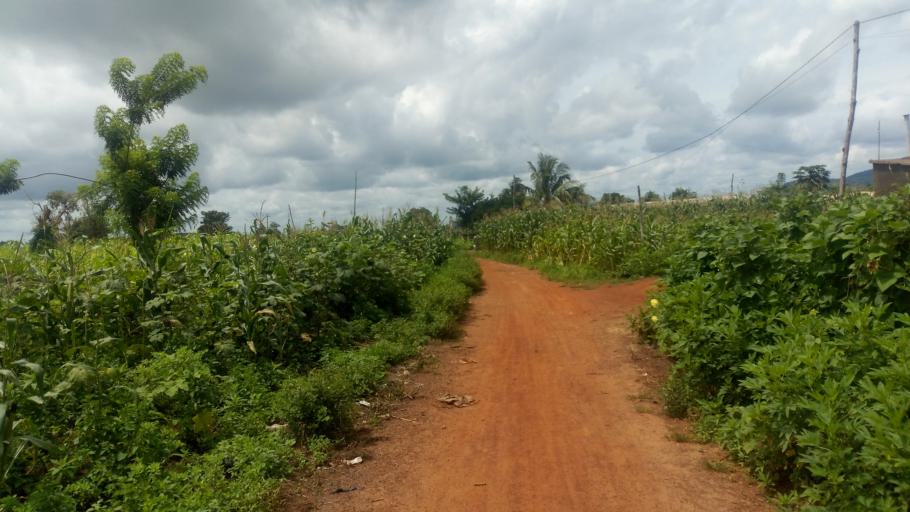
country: TG
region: Centrale
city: Sotouboua
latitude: 8.5548
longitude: 1.0034
